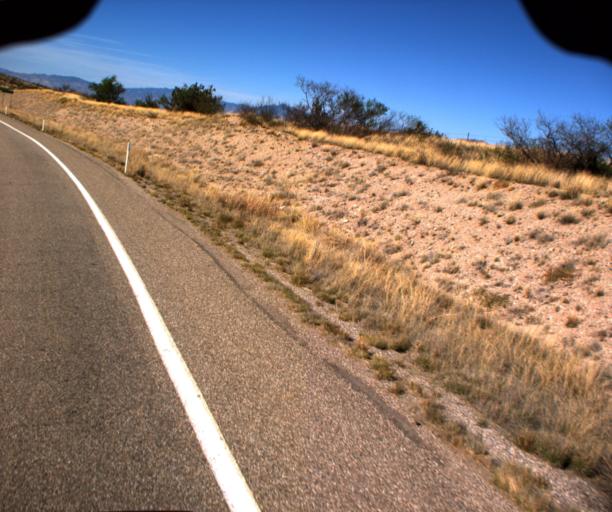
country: US
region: Arizona
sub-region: Pima County
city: Corona de Tucson
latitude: 31.8342
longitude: -110.7015
